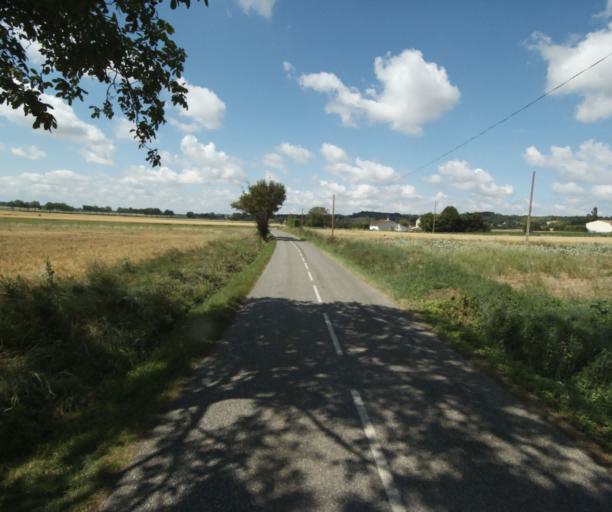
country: FR
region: Midi-Pyrenees
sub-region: Departement de la Haute-Garonne
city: Saint-Felix-Lauragais
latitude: 43.4554
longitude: 1.9232
